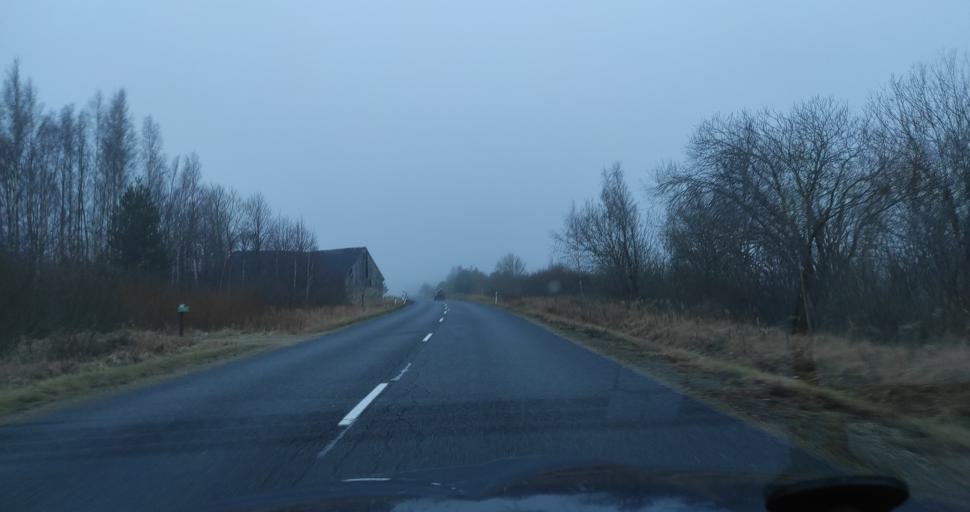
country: LV
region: Alsunga
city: Alsunga
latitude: 57.1138
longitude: 21.4230
